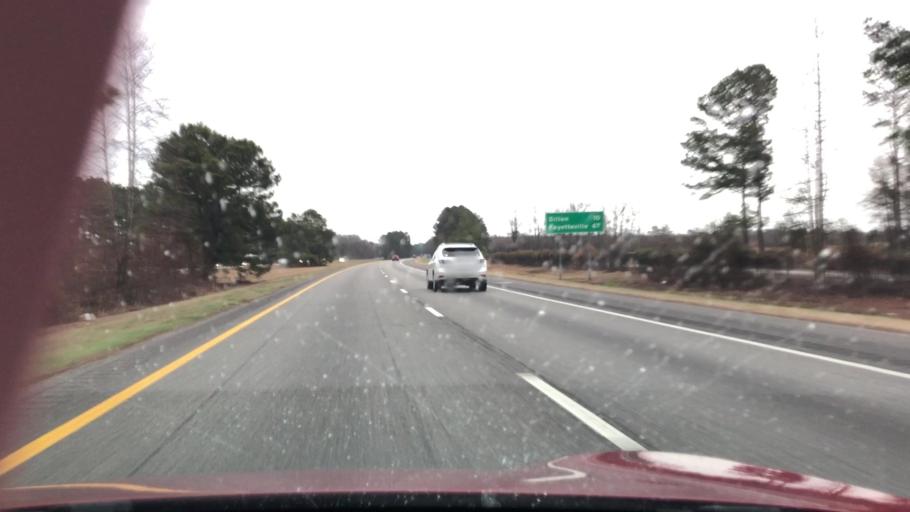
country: US
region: South Carolina
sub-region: Dillon County
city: Latta
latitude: 34.3518
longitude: -79.5215
